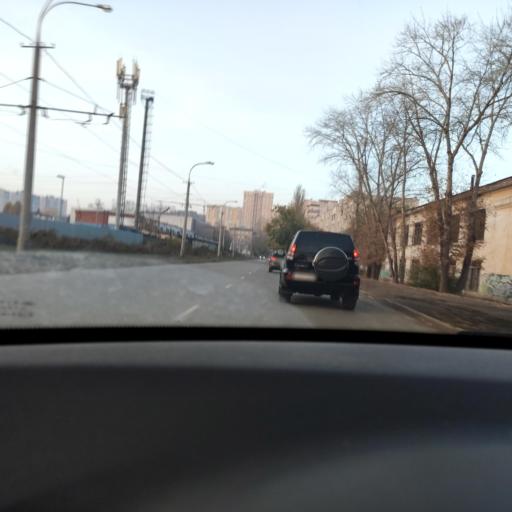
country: RU
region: Samara
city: Samara
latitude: 53.2116
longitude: 50.1870
